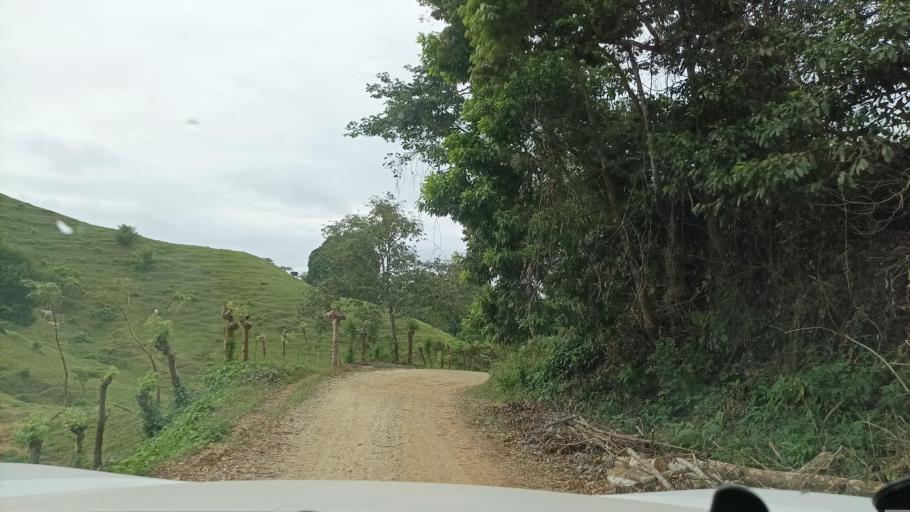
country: MX
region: Veracruz
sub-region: Uxpanapa
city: Poblado 10
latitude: 17.5708
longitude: -94.4228
